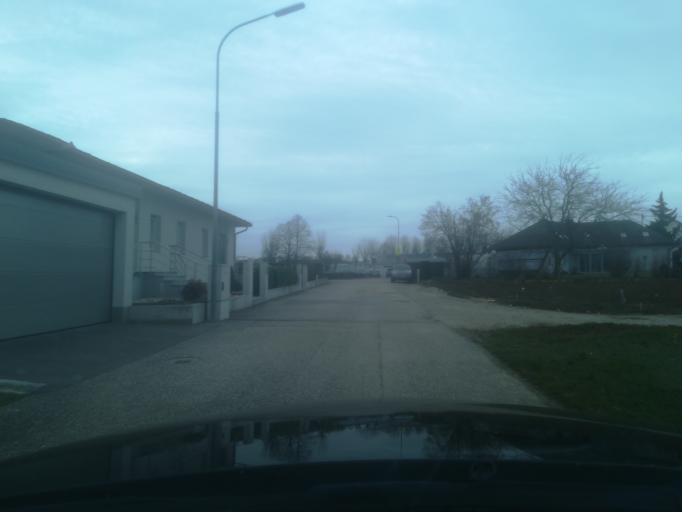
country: AT
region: Upper Austria
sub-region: Politischer Bezirk Linz-Land
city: Horsching
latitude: 48.2204
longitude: 14.1793
